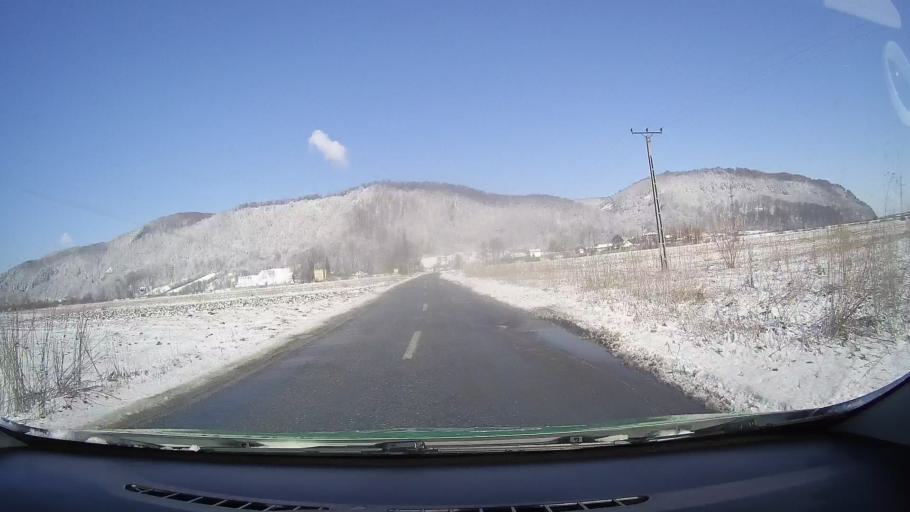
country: RO
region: Sibiu
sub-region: Comuna Turnu Rosu
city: Turnu Rosu
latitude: 45.6572
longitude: 24.2973
